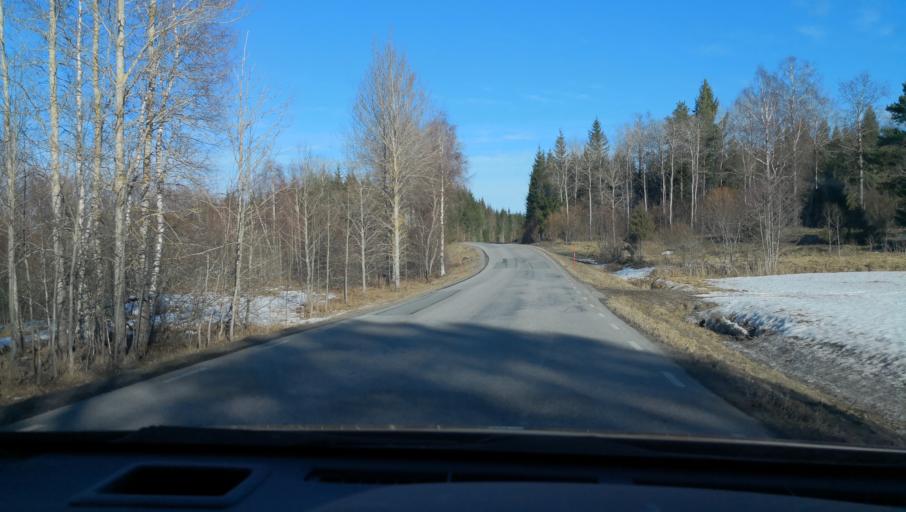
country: SE
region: Uppsala
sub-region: Osthammars Kommun
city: Osterbybruk
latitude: 60.2407
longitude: 17.9264
